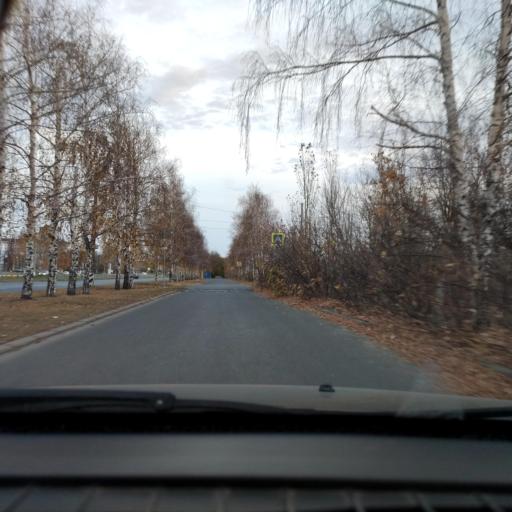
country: RU
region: Samara
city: Tol'yatti
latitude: 53.5023
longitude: 49.2610
